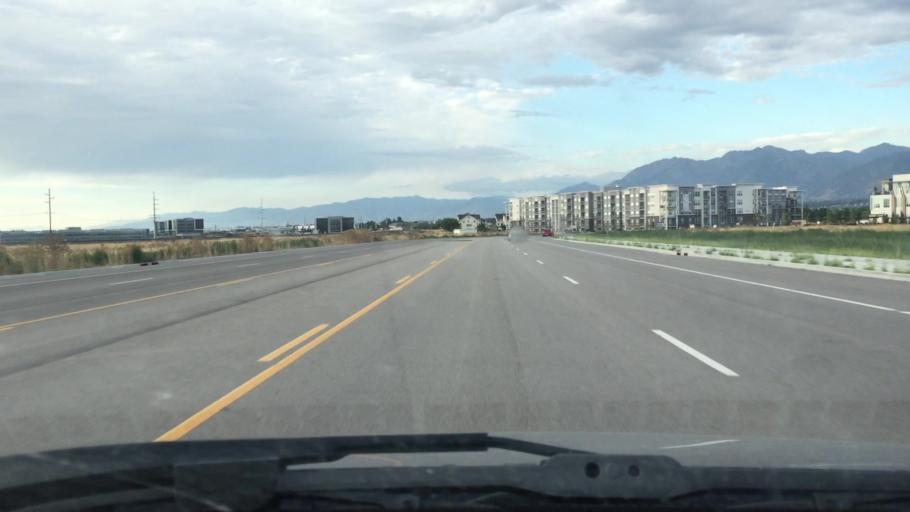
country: US
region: Utah
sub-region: Salt Lake County
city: Bluffdale
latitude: 40.5037
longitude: -111.9071
